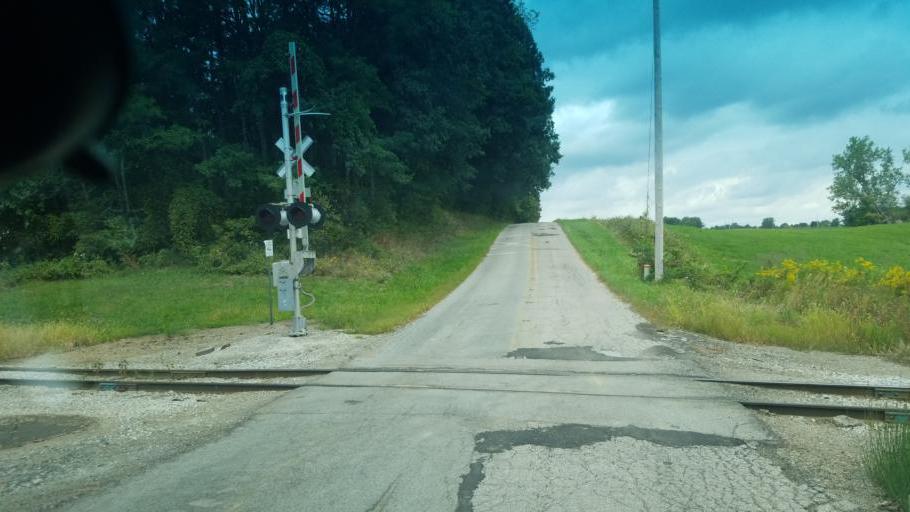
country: US
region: Ohio
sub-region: Richland County
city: Ontario
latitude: 40.8090
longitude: -82.5710
